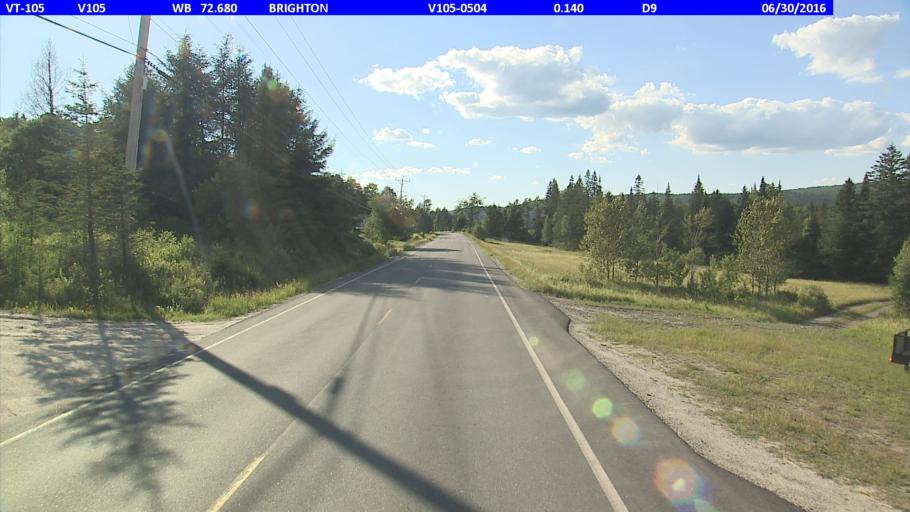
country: US
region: Vermont
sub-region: Caledonia County
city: Lyndonville
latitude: 44.8127
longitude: -71.9439
